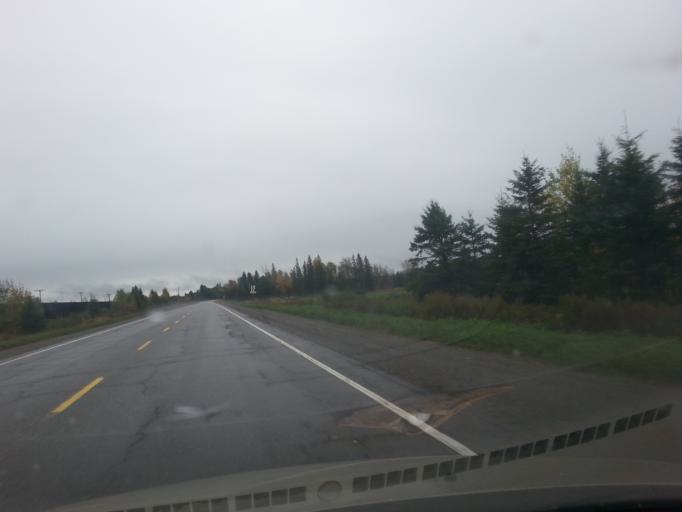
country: CA
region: Ontario
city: Greater Sudbury
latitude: 46.4380
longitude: -80.2886
